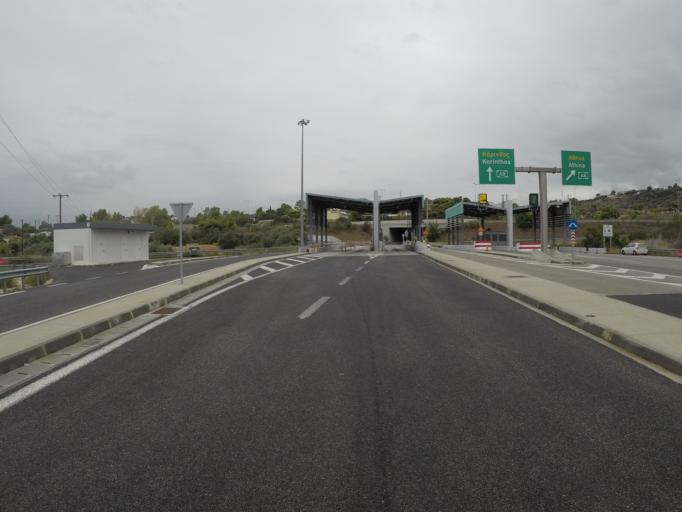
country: GR
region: Peloponnese
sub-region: Nomos Korinthias
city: Agioi Theodoroi
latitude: 37.9216
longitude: 23.1201
